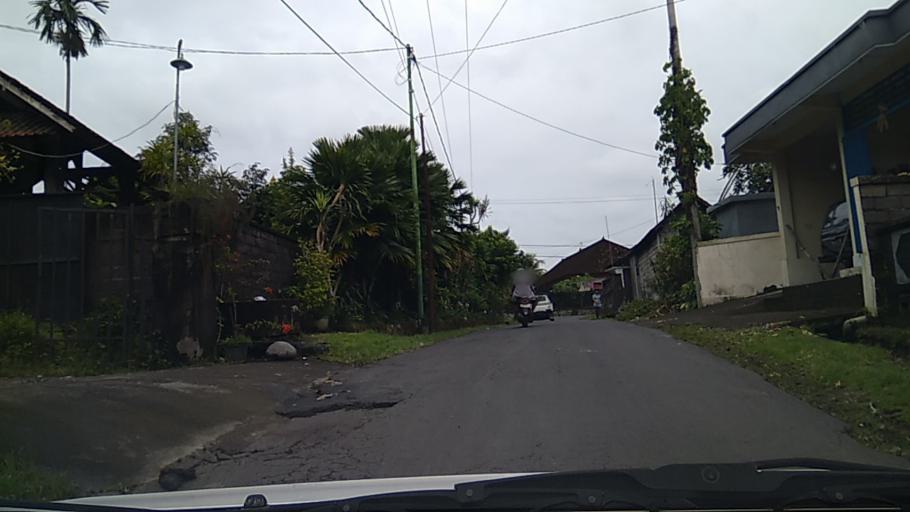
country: ID
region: Bali
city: Banjar Keraman
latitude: -8.5230
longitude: 115.2176
